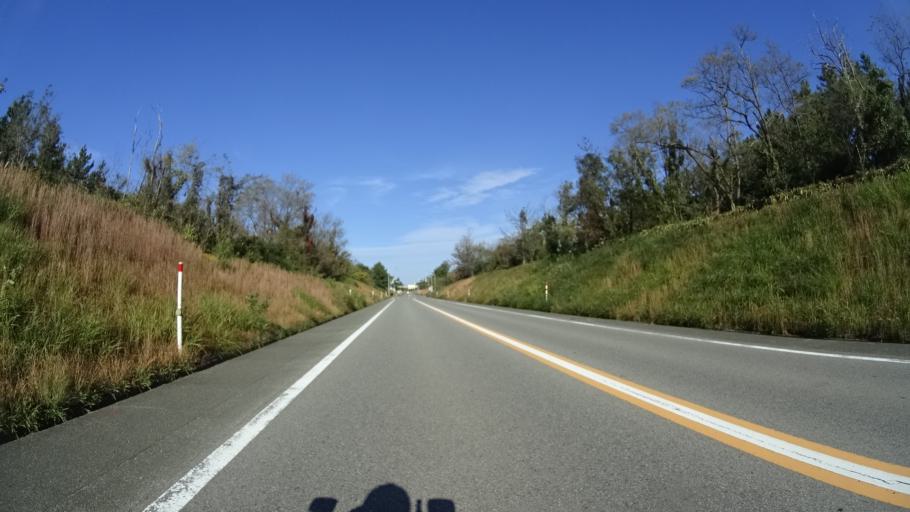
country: JP
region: Ishikawa
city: Kanazawa-shi
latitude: 36.6389
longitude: 136.6310
